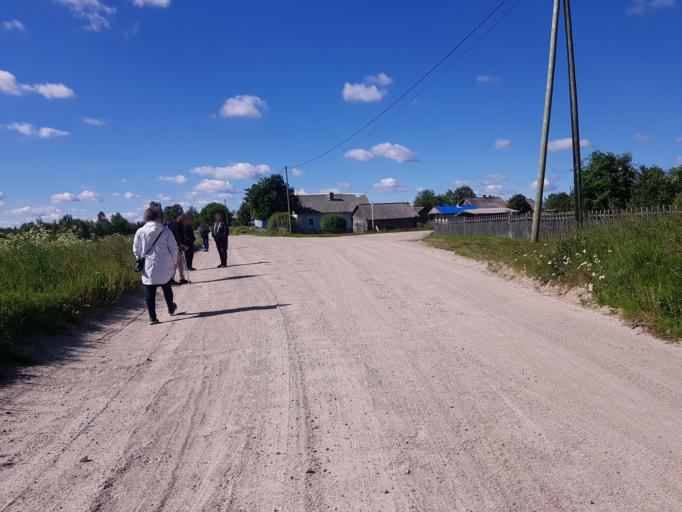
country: RU
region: Republic of Karelia
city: Yushkozero
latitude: 64.7507
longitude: 32.1080
